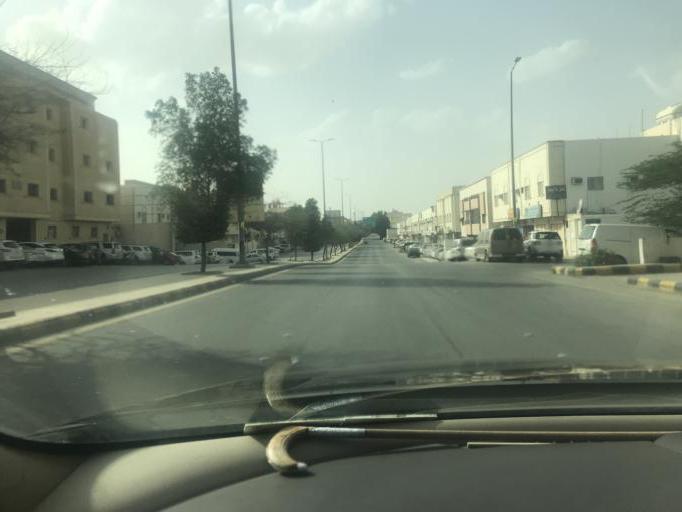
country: SA
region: Ar Riyad
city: Riyadh
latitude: 24.7277
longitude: 46.7647
